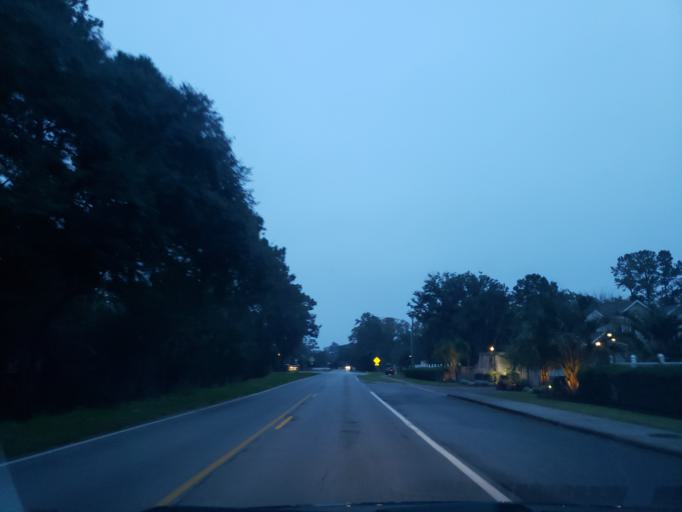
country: US
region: Georgia
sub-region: Chatham County
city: Wilmington Island
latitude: 32.0209
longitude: -80.9640
